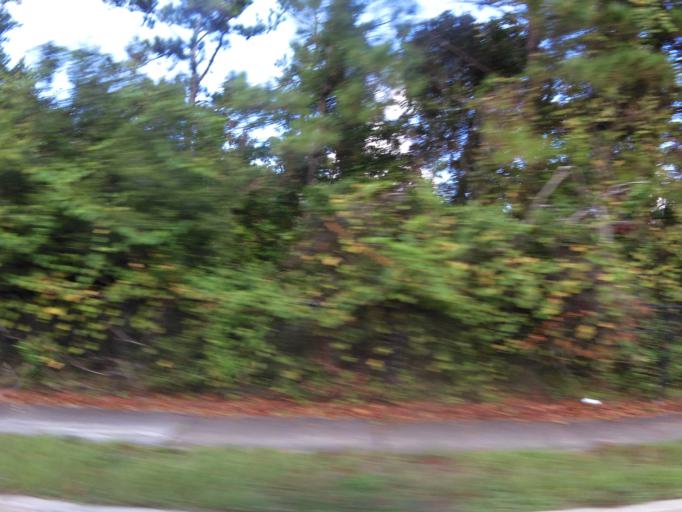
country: US
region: Florida
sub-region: Duval County
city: Jacksonville Beach
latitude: 30.2707
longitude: -81.4410
